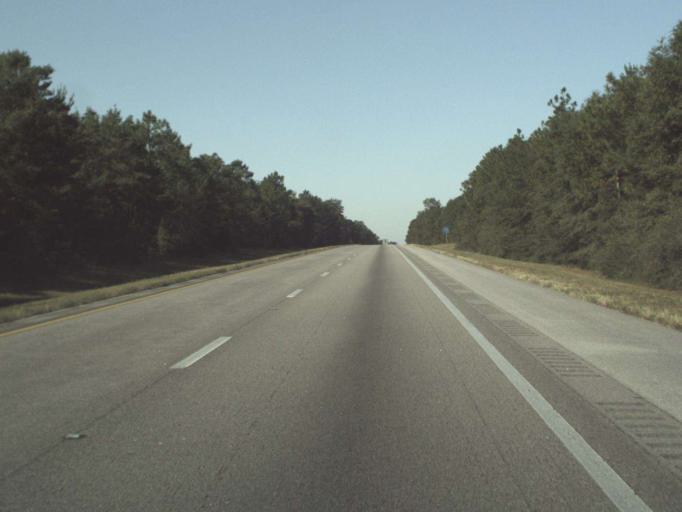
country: US
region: Florida
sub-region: Okaloosa County
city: Crestview
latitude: 30.7287
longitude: -86.3955
